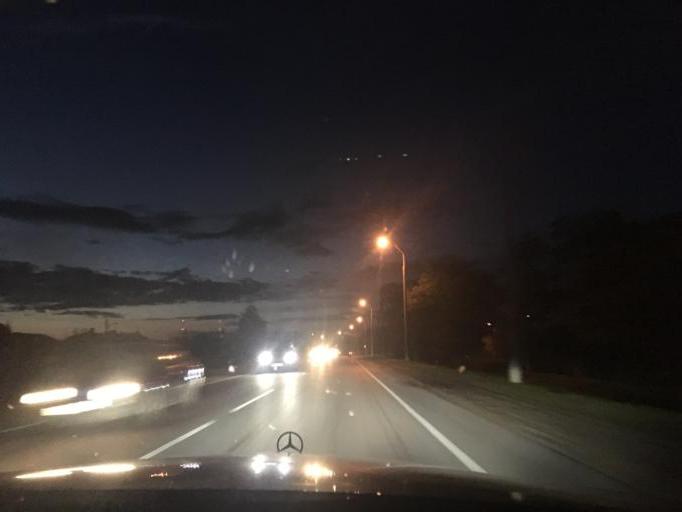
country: BY
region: Brest
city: Brest
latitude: 52.0660
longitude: 23.6861
